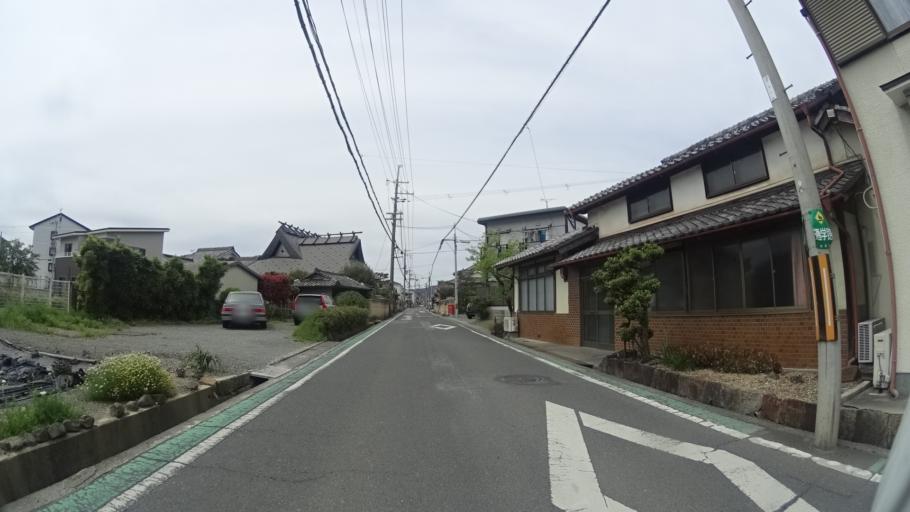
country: JP
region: Kyoto
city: Kameoka
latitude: 35.0292
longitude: 135.5583
